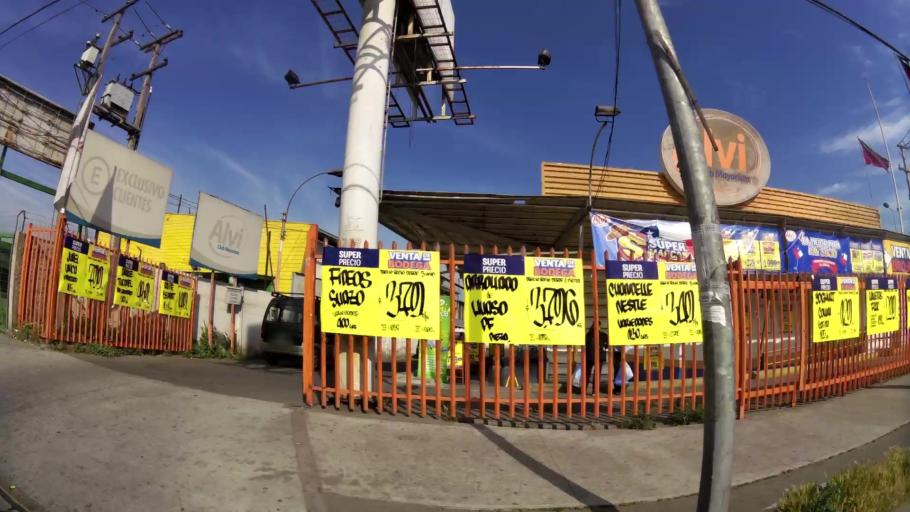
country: CL
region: Santiago Metropolitan
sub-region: Provincia de Santiago
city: La Pintana
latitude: -33.5466
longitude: -70.6337
